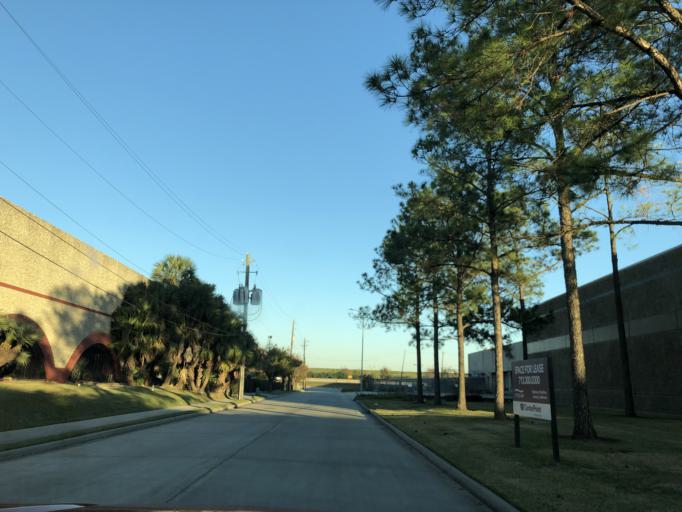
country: US
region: Texas
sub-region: Harris County
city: Jacinto City
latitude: 29.7585
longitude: -95.2676
